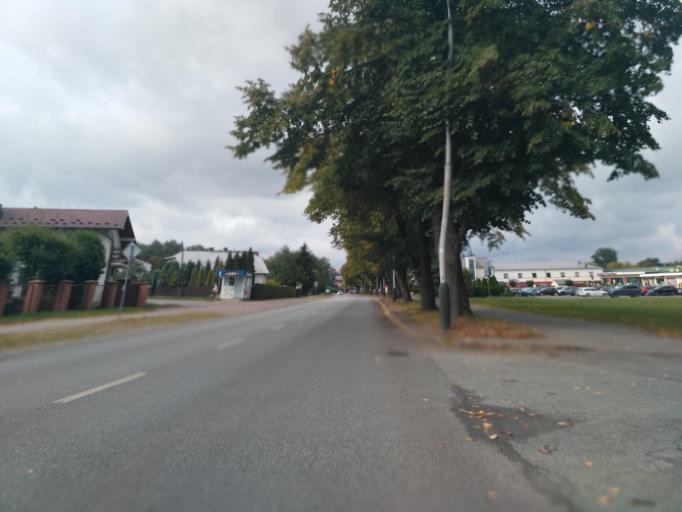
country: PL
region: Subcarpathian Voivodeship
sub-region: Krosno
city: Krosno
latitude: 49.6912
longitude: 21.7771
